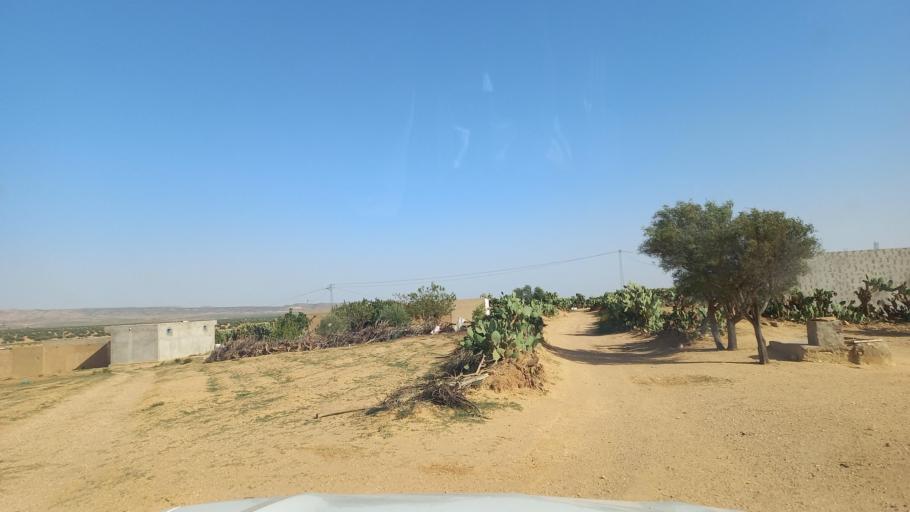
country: TN
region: Al Qasrayn
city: Sbiba
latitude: 35.3194
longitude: 9.0221
